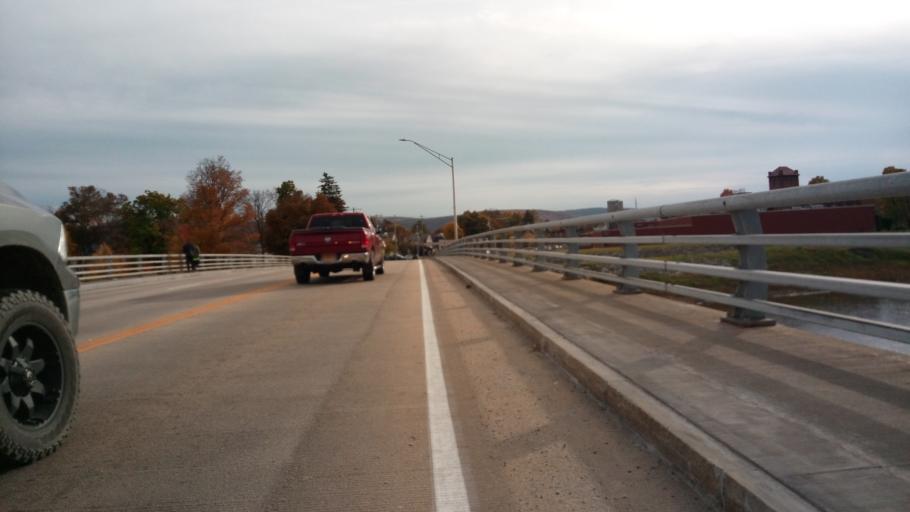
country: US
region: New York
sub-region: Chemung County
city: Elmira
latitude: 42.0877
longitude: -76.7981
